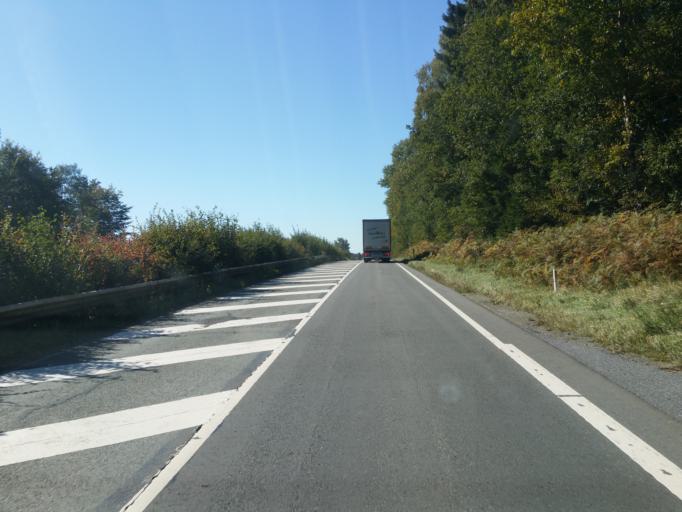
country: BE
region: Wallonia
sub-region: Province du Luxembourg
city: Bertrix
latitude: 49.8829
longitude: 5.2736
